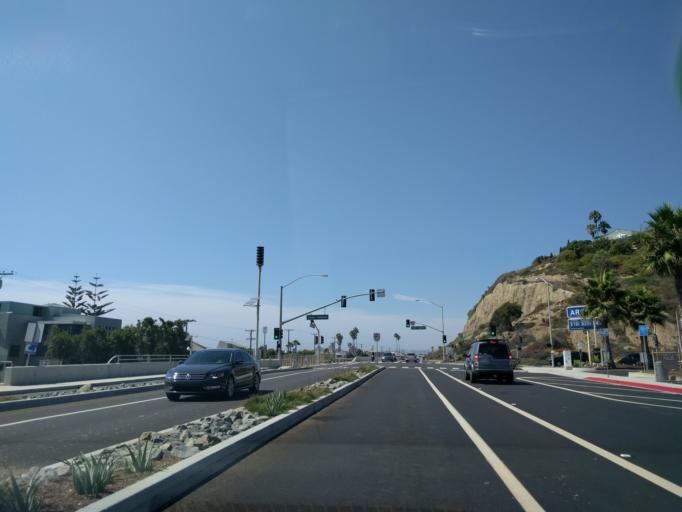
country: US
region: California
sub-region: Orange County
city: San Clemente
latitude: 33.4412
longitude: -117.6446
